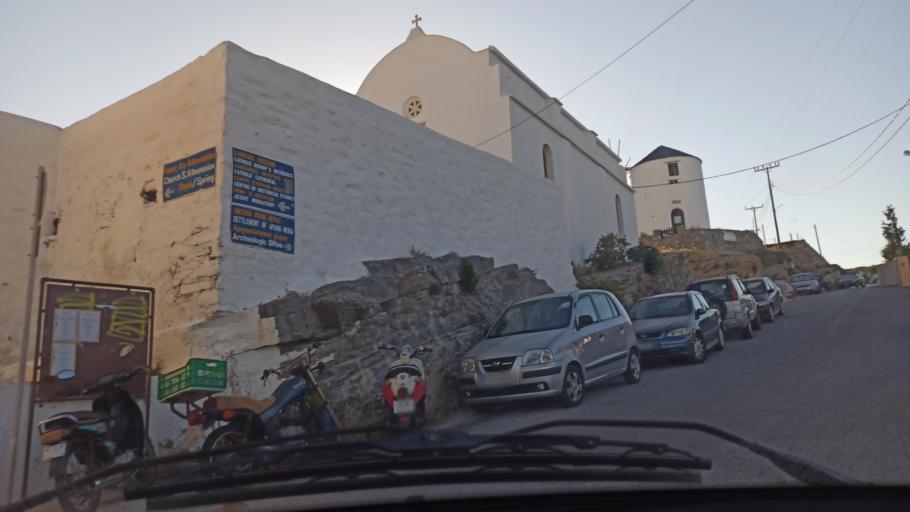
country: GR
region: South Aegean
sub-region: Nomos Kykladon
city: Ano Syros
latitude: 37.4523
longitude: 24.9350
